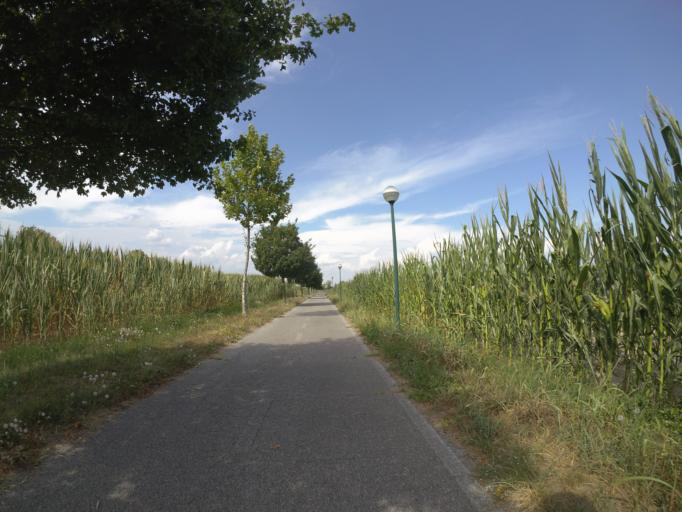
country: IT
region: Friuli Venezia Giulia
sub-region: Provincia di Udine
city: Lignano Sabbiadoro
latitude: 45.6688
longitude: 13.0704
